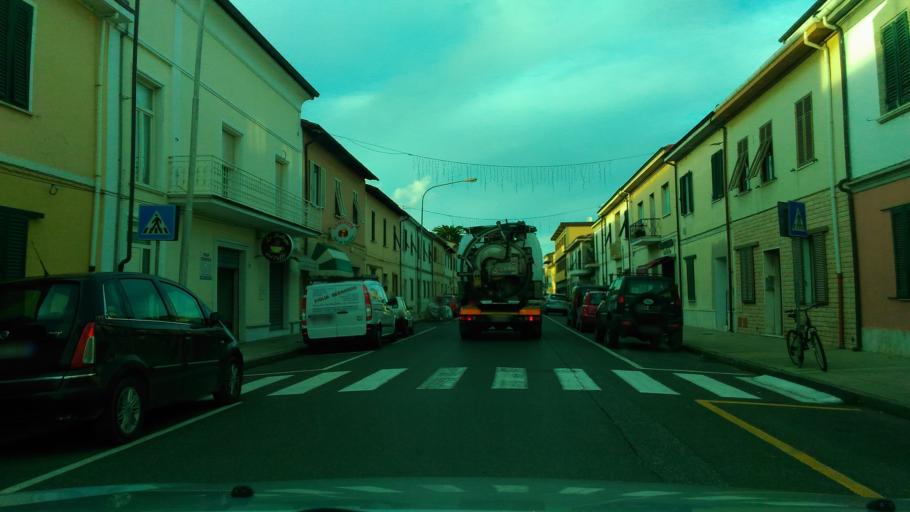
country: IT
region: Tuscany
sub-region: Provincia di Livorno
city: S.P. in Palazzi
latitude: 43.3243
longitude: 10.5092
